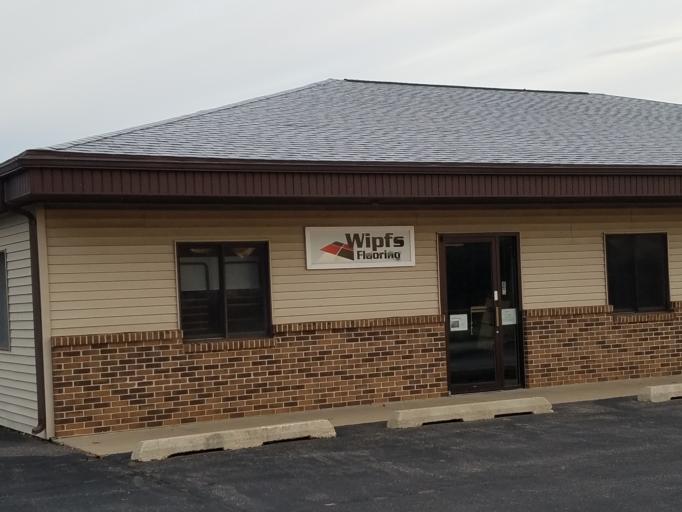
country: US
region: Wisconsin
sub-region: Vernon County
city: Hillsboro
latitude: 43.6550
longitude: -90.3353
